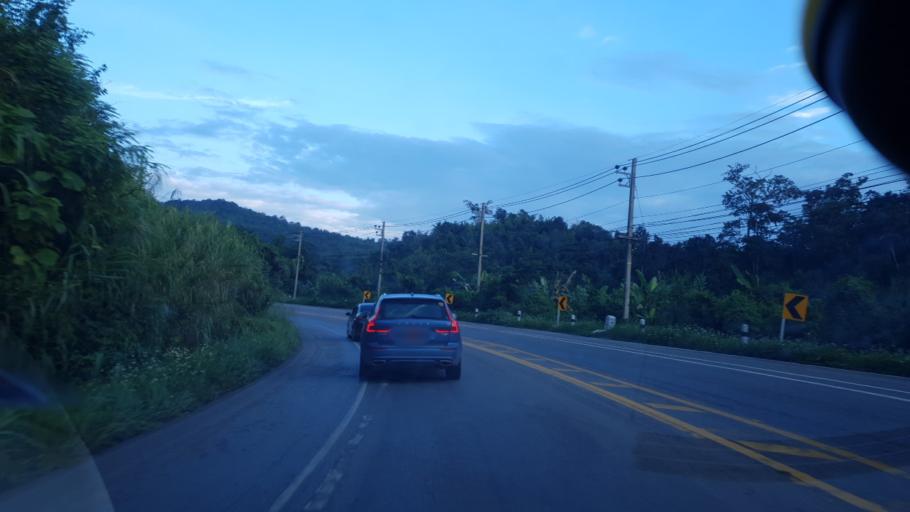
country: TH
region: Chiang Rai
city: Mae Suai
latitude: 19.6714
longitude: 99.5603
